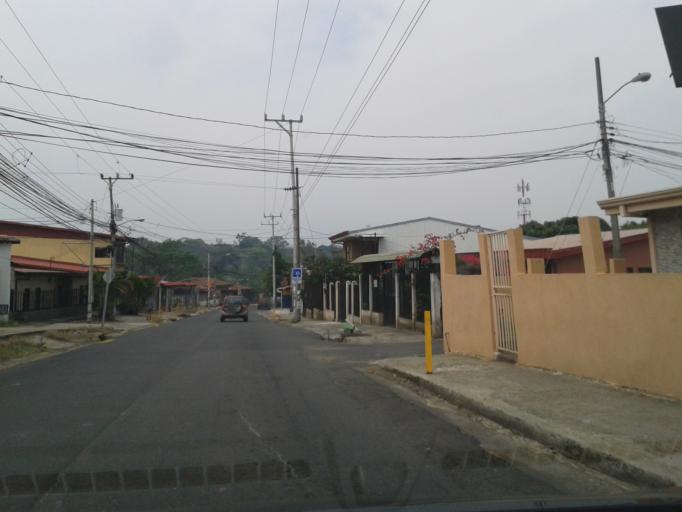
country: CR
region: Heredia
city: San Francisco
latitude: 9.9748
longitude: -84.1391
